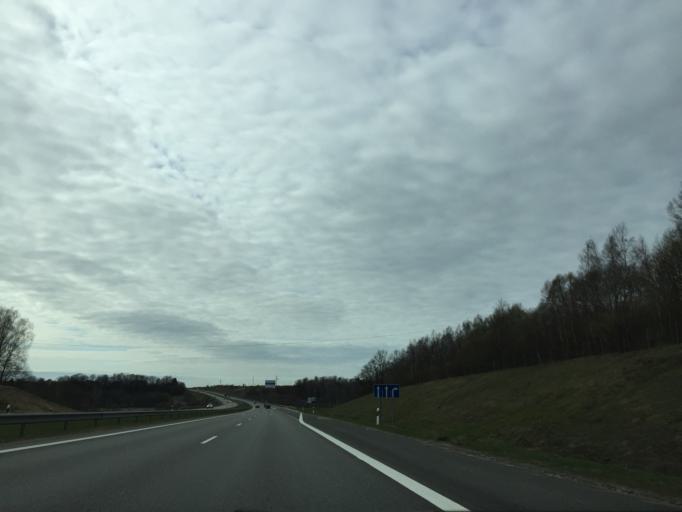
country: LT
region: Klaipedos apskritis
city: Gargzdai
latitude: 55.7257
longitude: 21.4217
